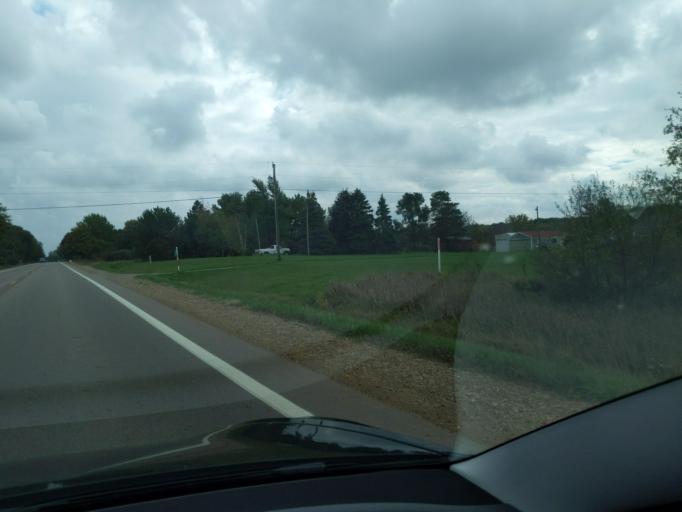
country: US
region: Michigan
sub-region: Eaton County
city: Eaton Rapids
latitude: 42.5368
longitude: -84.7278
